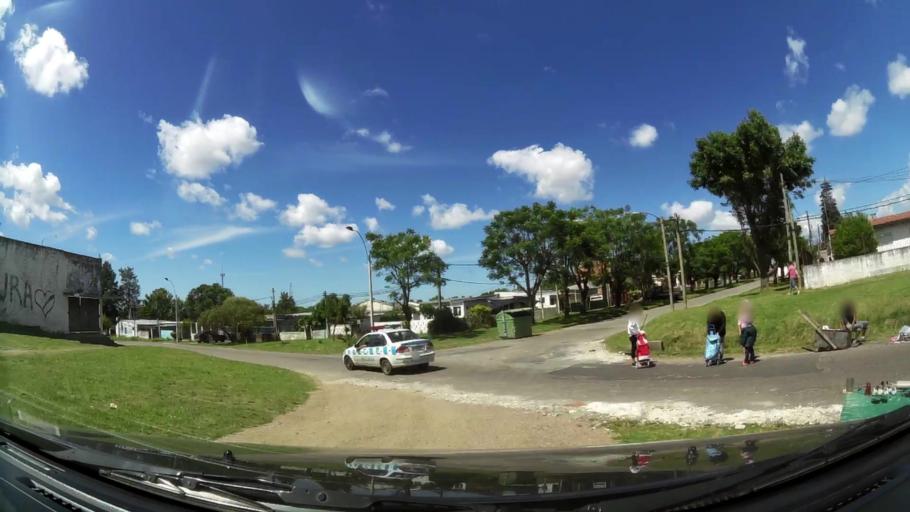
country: UY
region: Canelones
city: Paso de Carrasco
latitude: -34.8387
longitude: -56.1334
